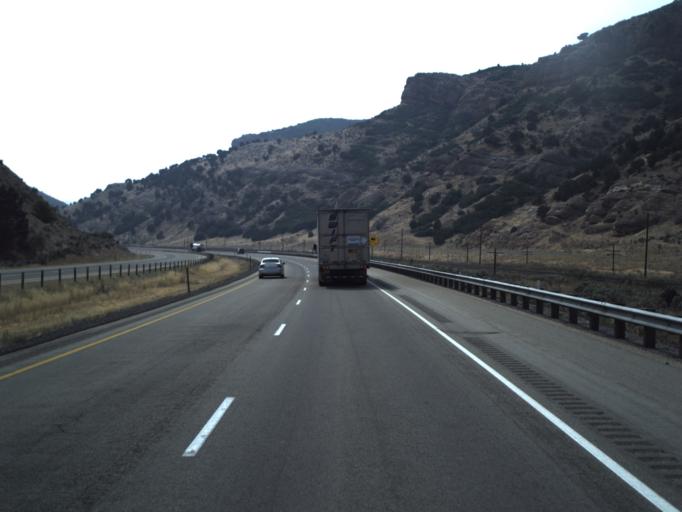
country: US
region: Utah
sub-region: Summit County
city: Coalville
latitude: 41.0202
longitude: -111.3632
